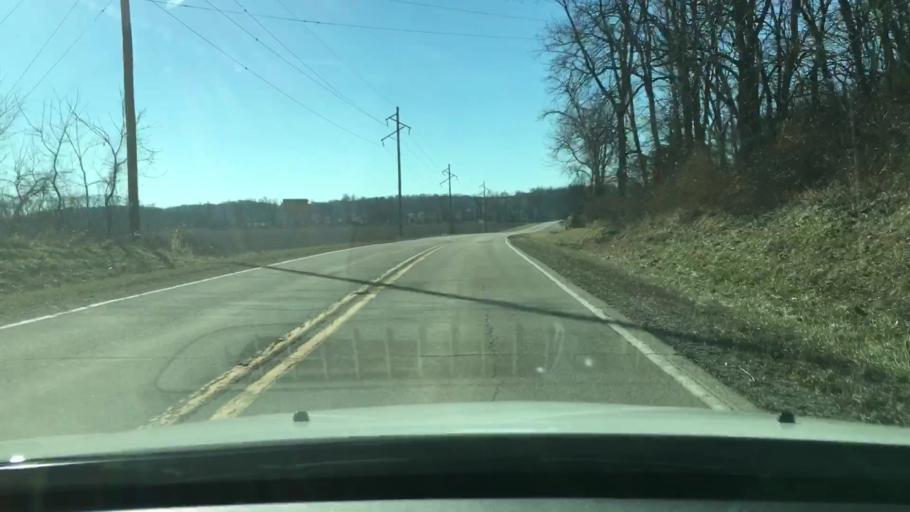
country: US
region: Illinois
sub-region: Mason County
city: Havana
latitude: 40.2318
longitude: -90.1982
